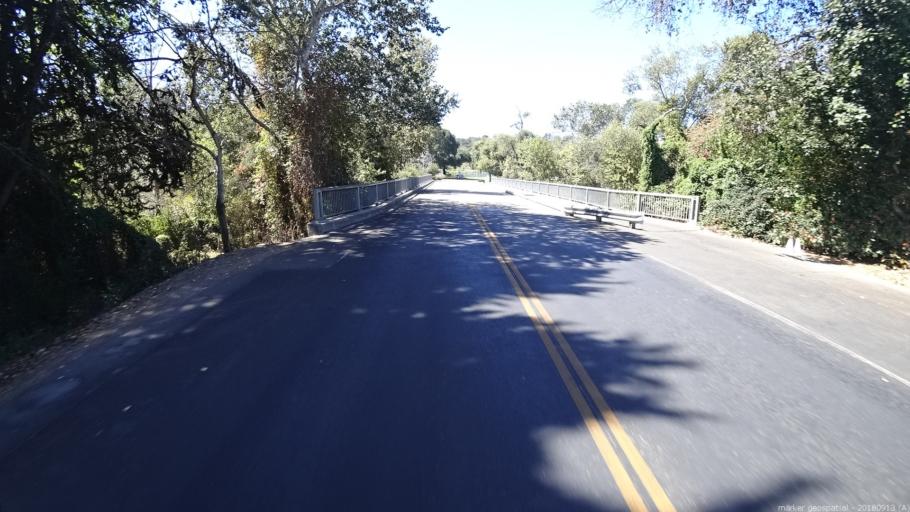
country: US
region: California
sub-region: Monterey County
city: Del Rey Oaks
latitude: 36.5305
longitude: -121.8573
